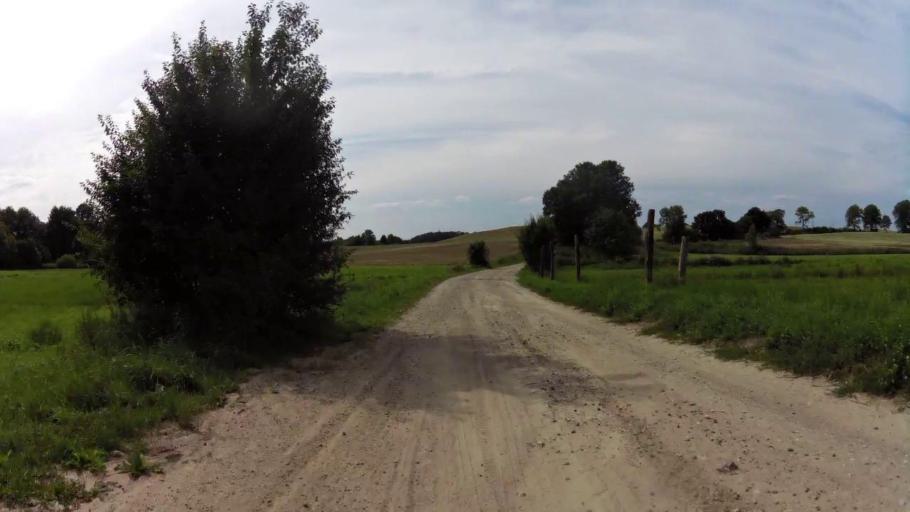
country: PL
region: West Pomeranian Voivodeship
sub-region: Powiat lobeski
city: Wegorzyno
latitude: 53.5388
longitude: 15.6046
